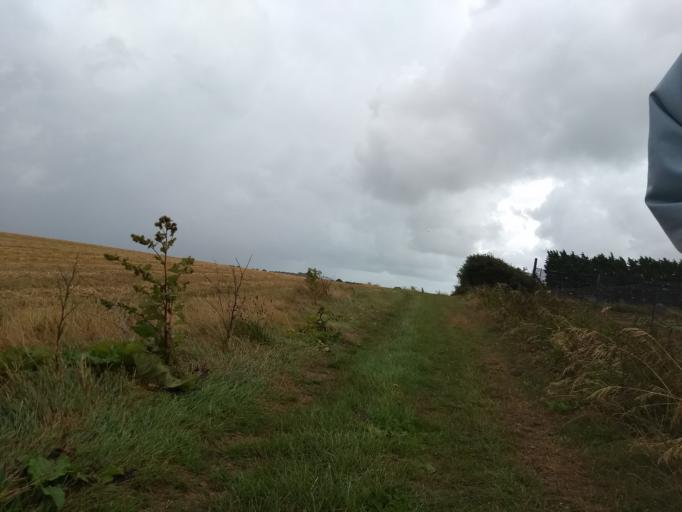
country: GB
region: England
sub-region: Isle of Wight
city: Newchurch
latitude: 50.6386
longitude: -1.2194
